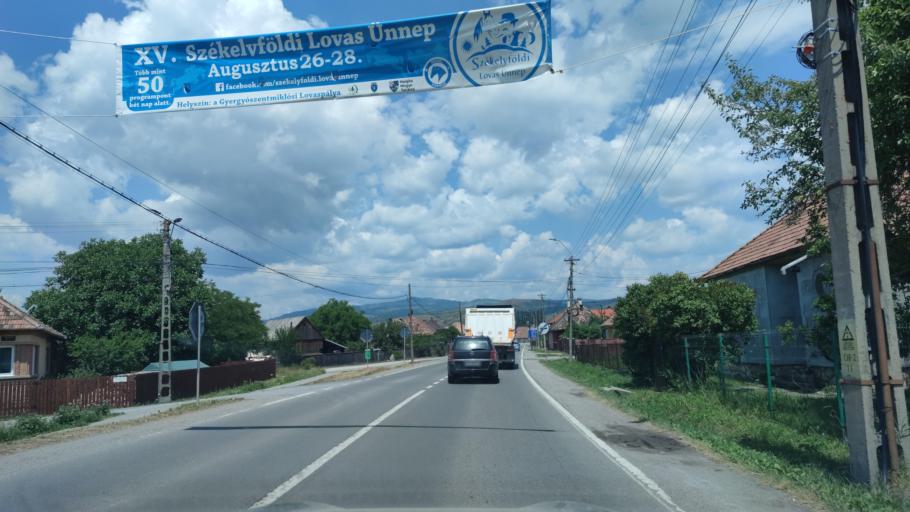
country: RO
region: Harghita
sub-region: Municipiul Gheorgheni
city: Gheorgheni
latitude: 46.7153
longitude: 25.6023
